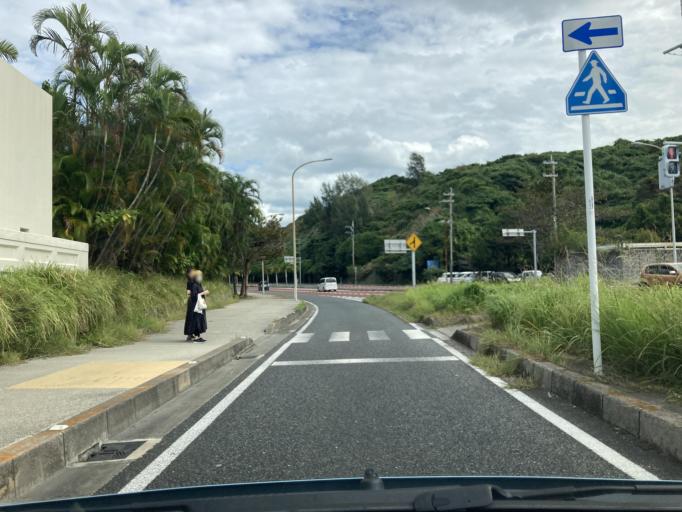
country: JP
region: Okinawa
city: Ishikawa
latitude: 26.4350
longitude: 127.7886
